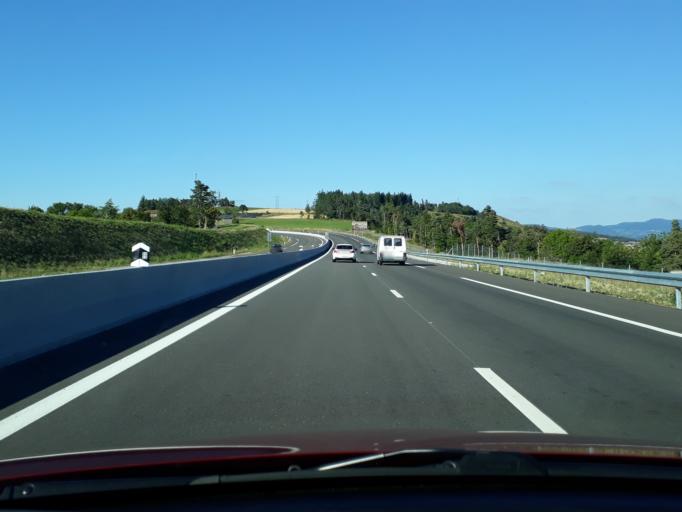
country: FR
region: Auvergne
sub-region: Departement de la Haute-Loire
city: Cussac-sur-Loire
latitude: 45.0035
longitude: 3.8808
